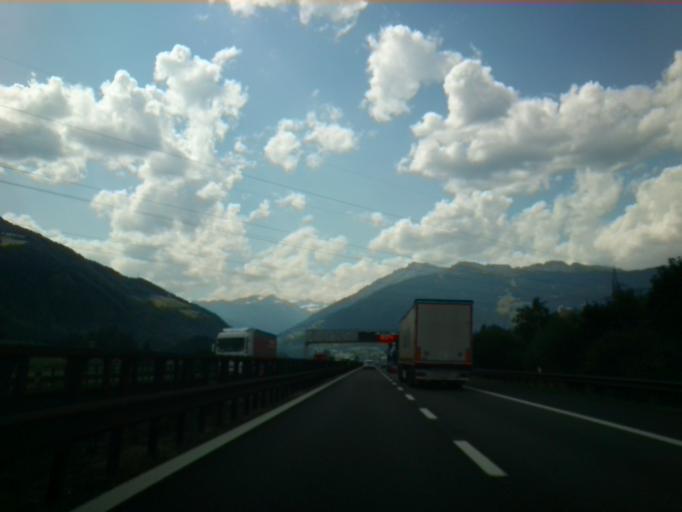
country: IT
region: Trentino-Alto Adige
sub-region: Bolzano
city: Campo di Trens
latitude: 46.8717
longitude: 11.4737
